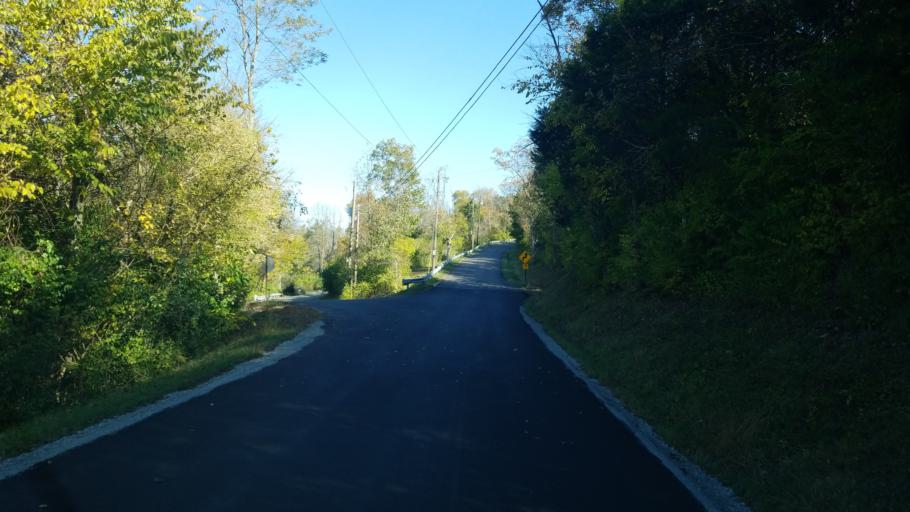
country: US
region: Ohio
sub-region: Warren County
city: Morrow
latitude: 39.3812
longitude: -84.0896
